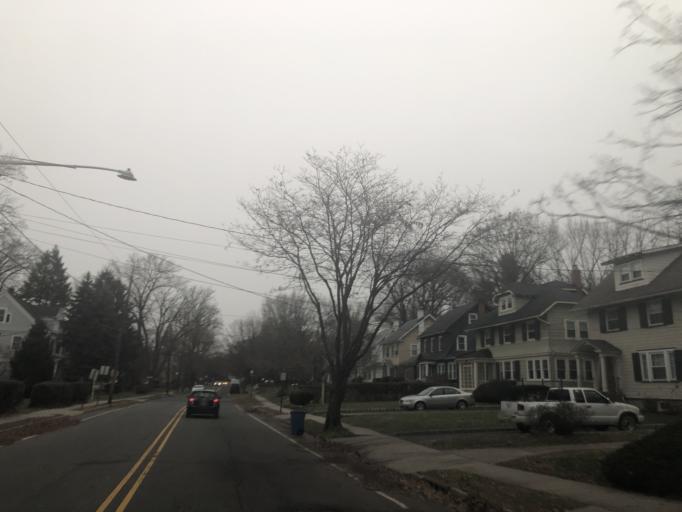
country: US
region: New Jersey
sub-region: Essex County
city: Maplewood
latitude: 40.7351
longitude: -74.2626
